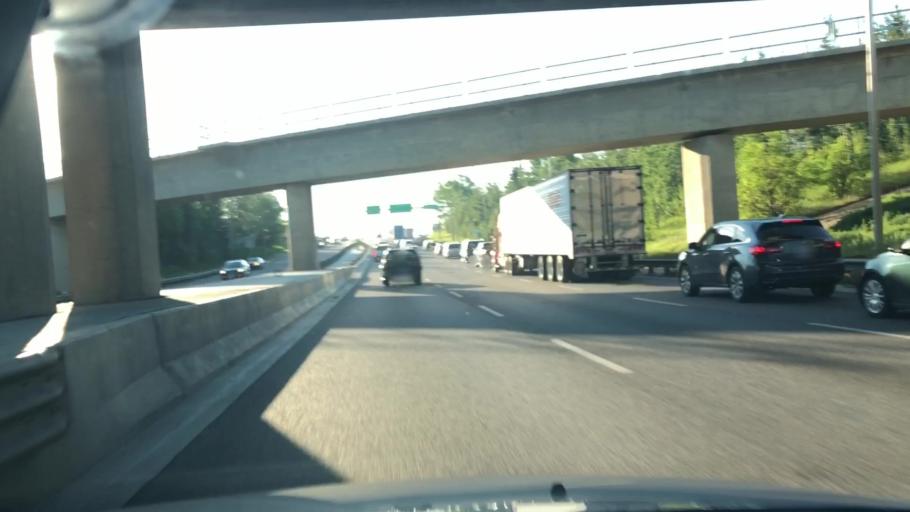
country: CA
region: Alberta
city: Edmonton
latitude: 53.5818
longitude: -113.5302
